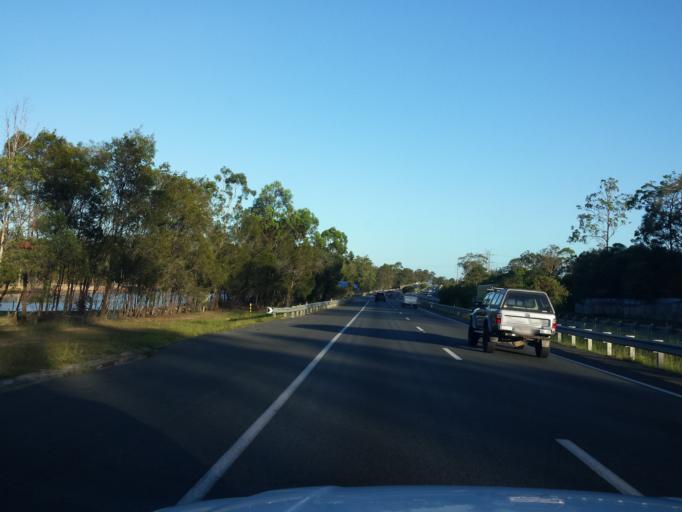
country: AU
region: Queensland
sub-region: Logan
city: Woodridge
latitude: -27.6579
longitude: 153.0846
